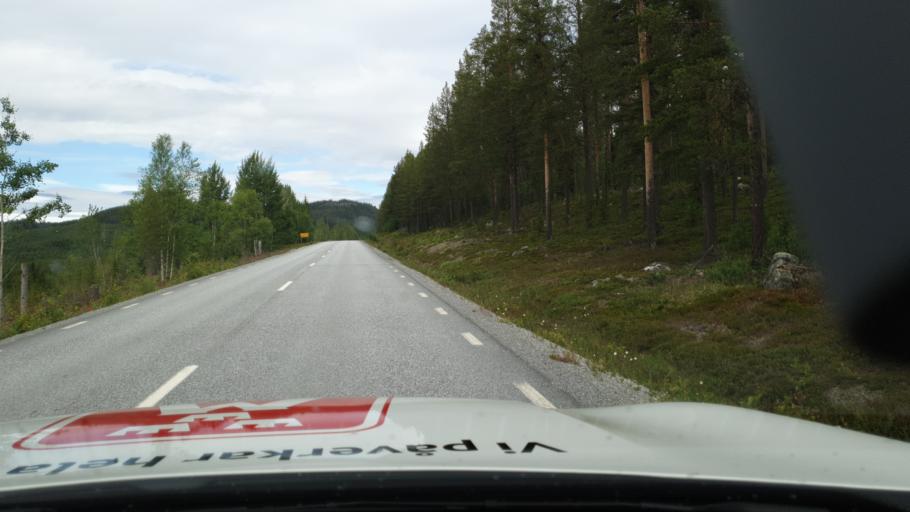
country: SE
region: Vaesterbotten
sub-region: Storumans Kommun
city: Fristad
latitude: 65.2688
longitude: 16.8239
